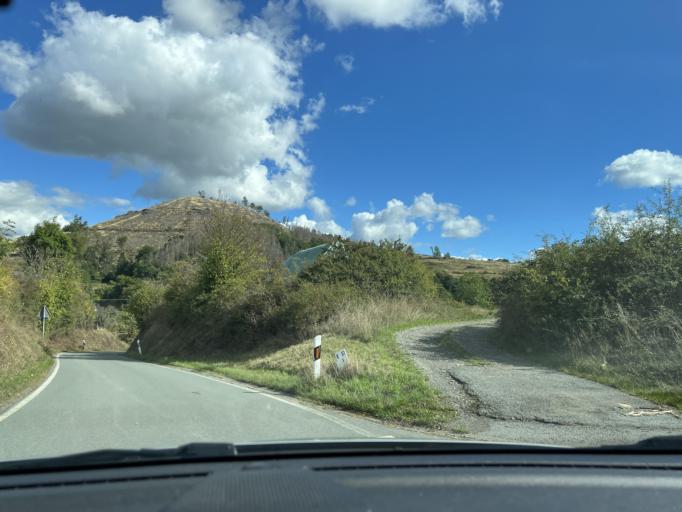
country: DE
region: North Rhine-Westphalia
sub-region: Regierungsbezirk Arnsberg
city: Bad Laasphe
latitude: 50.9834
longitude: 8.4598
